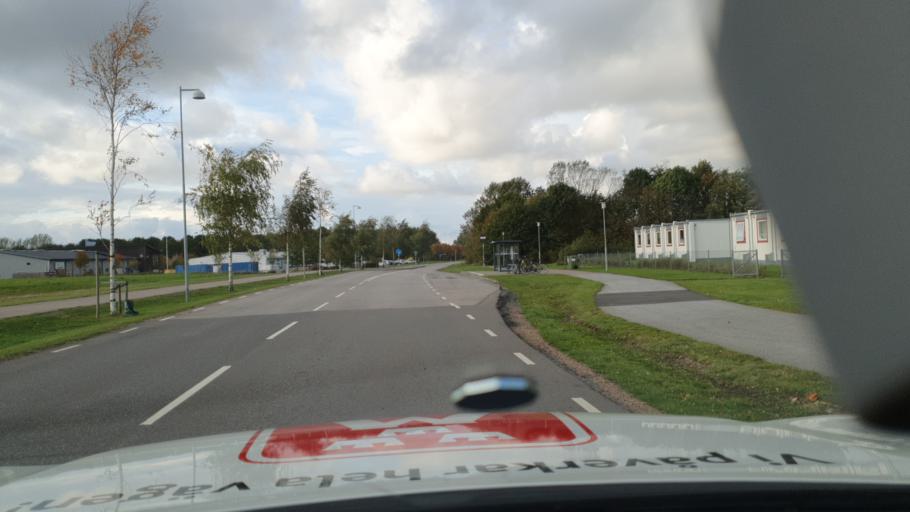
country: SE
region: Skane
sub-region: Vellinge Kommun
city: Vellinge
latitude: 55.4594
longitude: 13.0220
